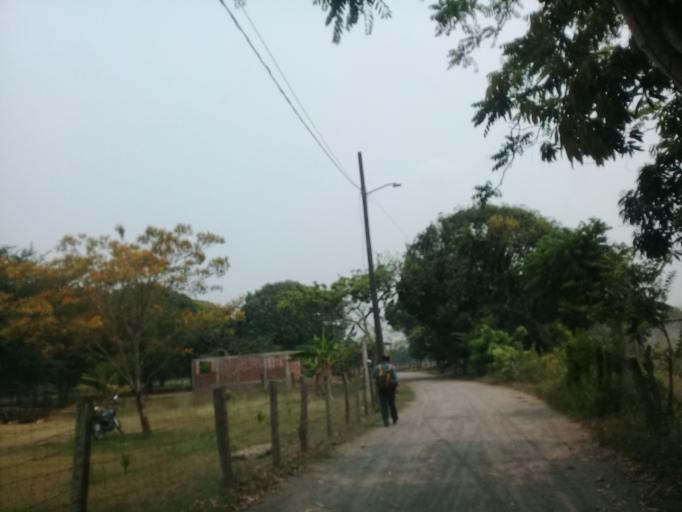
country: MX
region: Veracruz
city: Jamapa
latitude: 18.9525
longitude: -96.2055
